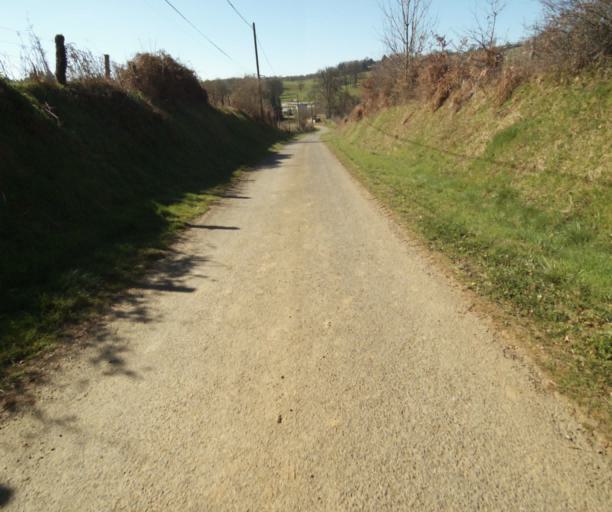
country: FR
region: Limousin
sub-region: Departement de la Correze
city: Seilhac
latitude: 45.3797
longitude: 1.7385
